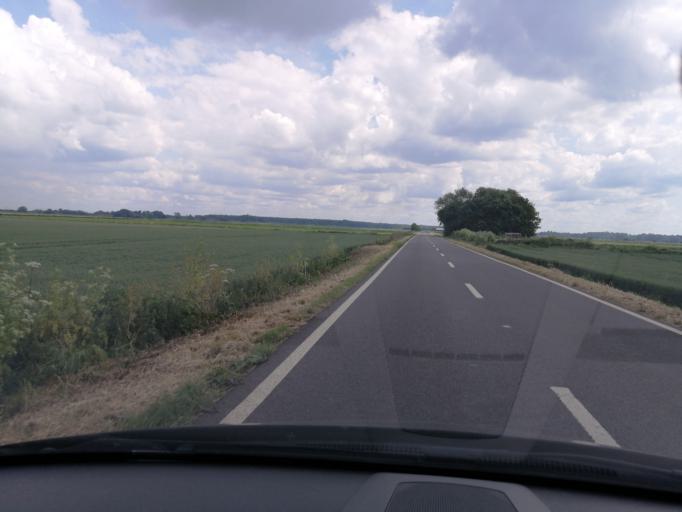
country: GB
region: England
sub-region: Cambridgeshire
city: Yaxley
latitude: 52.5064
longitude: -0.2571
